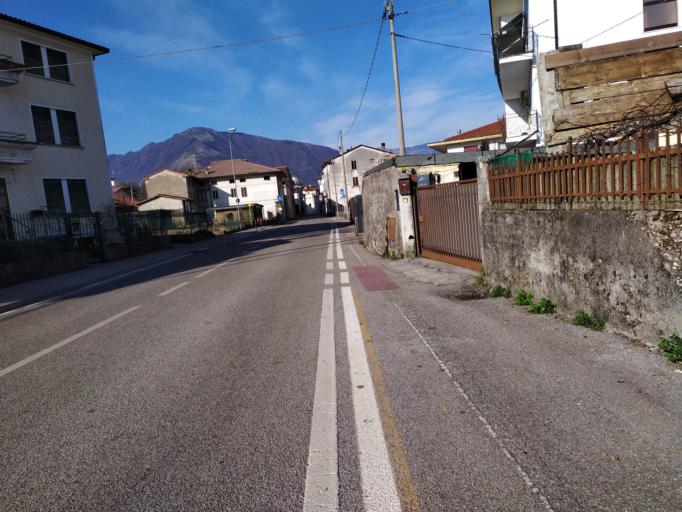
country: IT
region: Veneto
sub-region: Provincia di Vicenza
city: San Vito di Leguzzano
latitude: 45.7004
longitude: 11.3760
